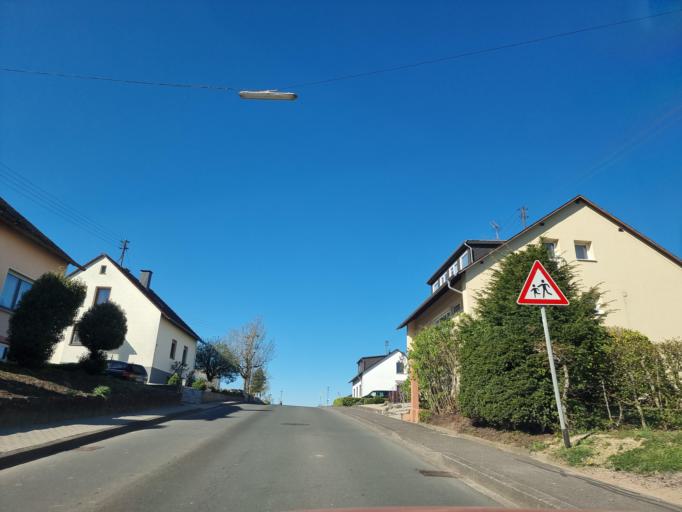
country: DE
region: Rheinland-Pfalz
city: Orenhofen
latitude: 49.8964
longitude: 6.6469
